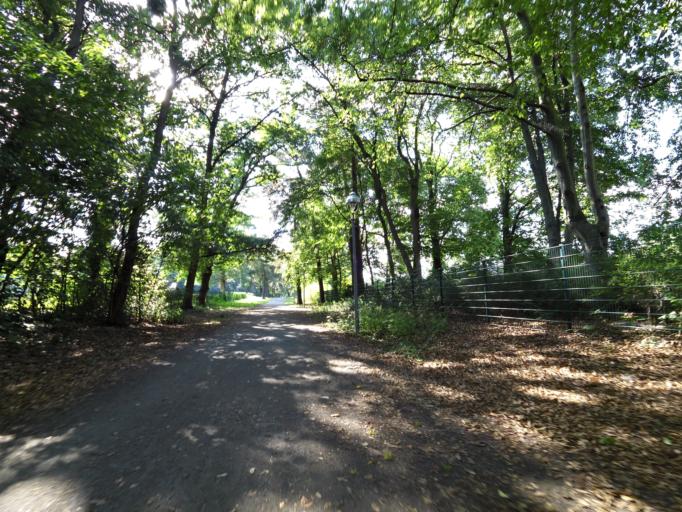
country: DE
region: Berlin
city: Zehlendorf Bezirk
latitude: 52.4463
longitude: 13.2507
